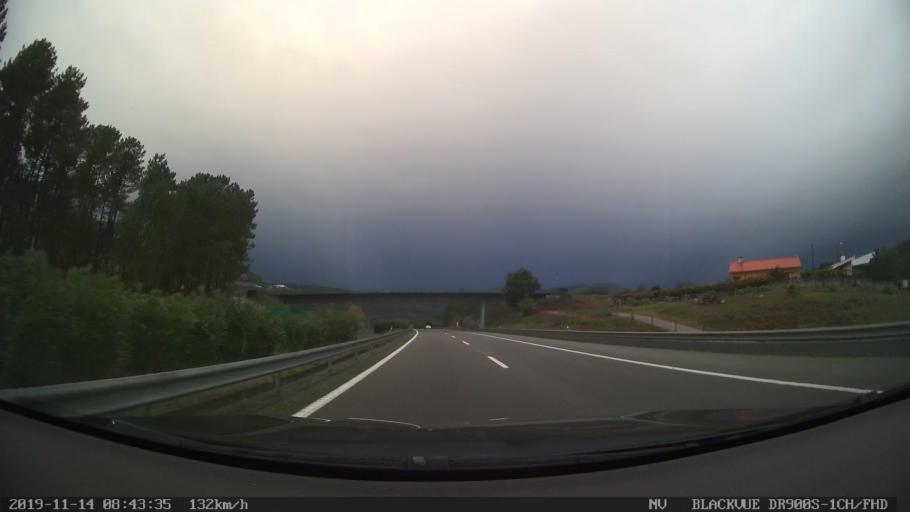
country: PT
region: Viana do Castelo
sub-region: Ponte de Lima
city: Ponte de Lima
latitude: 41.8040
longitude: -8.5866
